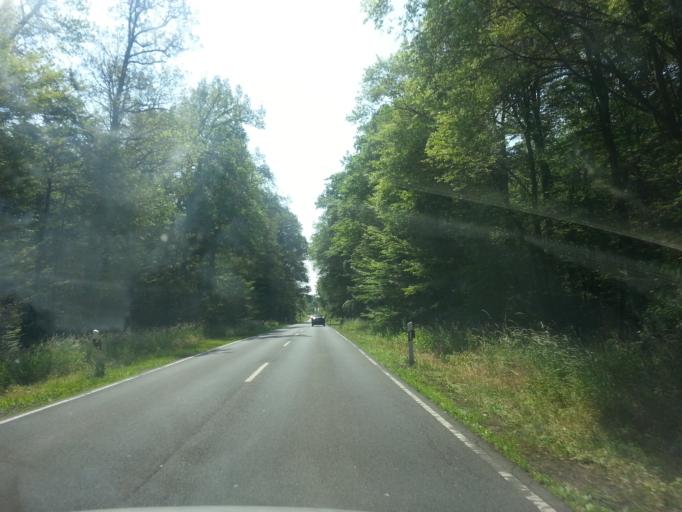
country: DE
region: Hesse
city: Dreieich
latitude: 50.0233
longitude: 8.7243
